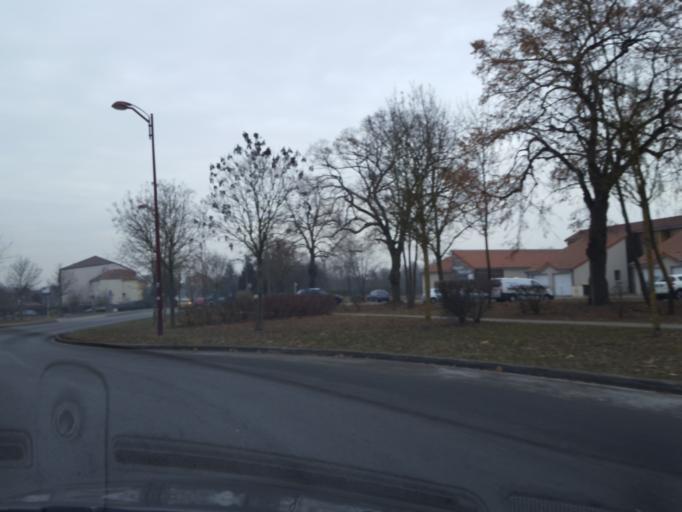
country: FR
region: Lorraine
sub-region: Departement de la Moselle
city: Moulins-les-Metz
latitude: 49.0905
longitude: 6.1221
